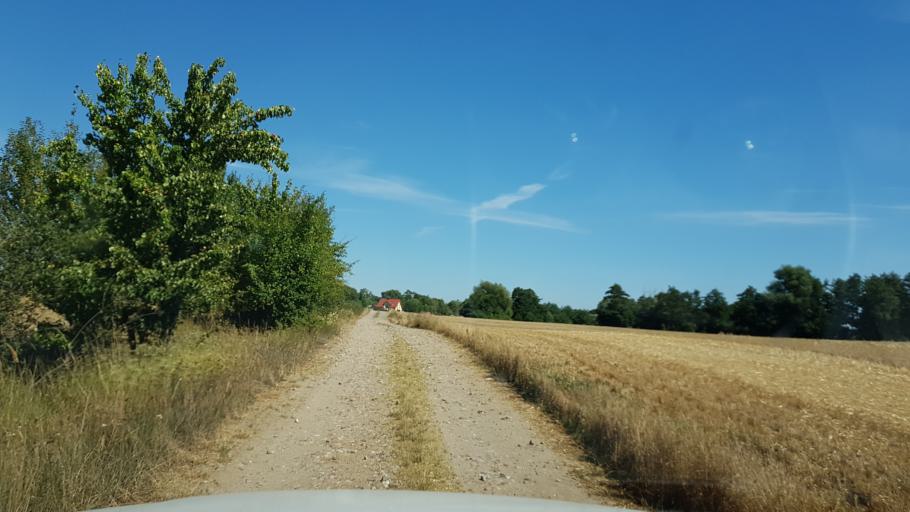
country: PL
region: West Pomeranian Voivodeship
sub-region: Powiat gryfinski
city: Moryn
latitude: 52.8993
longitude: 14.4055
